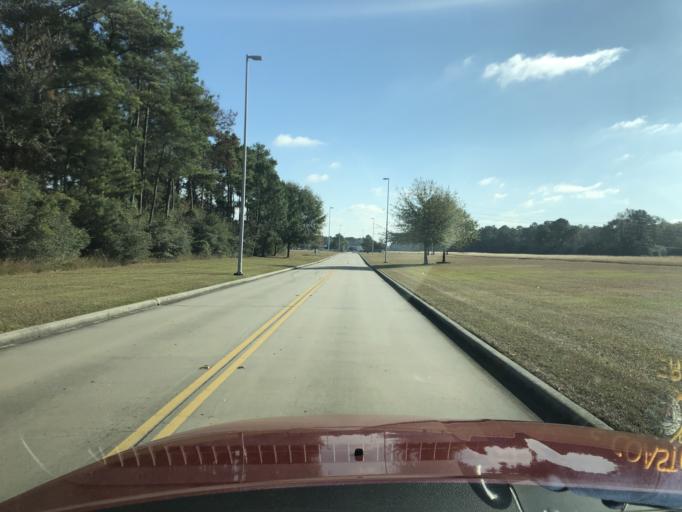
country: US
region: Texas
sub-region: Harris County
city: Aldine
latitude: 29.9667
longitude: -95.3317
